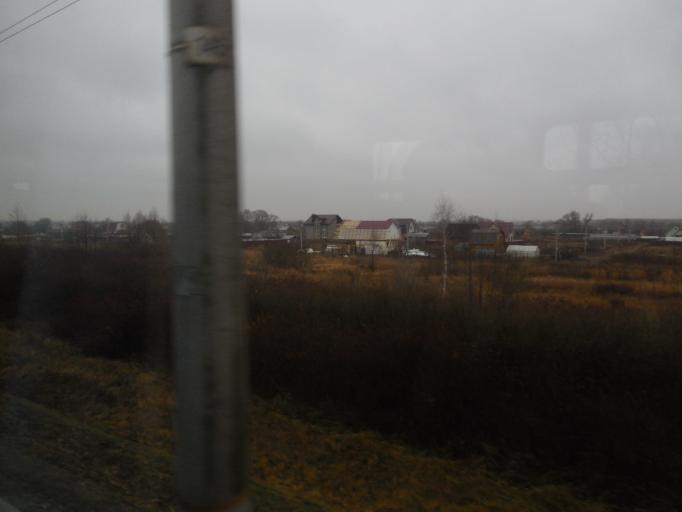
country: RU
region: Moskovskaya
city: Yam
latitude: 55.5074
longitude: 37.7193
